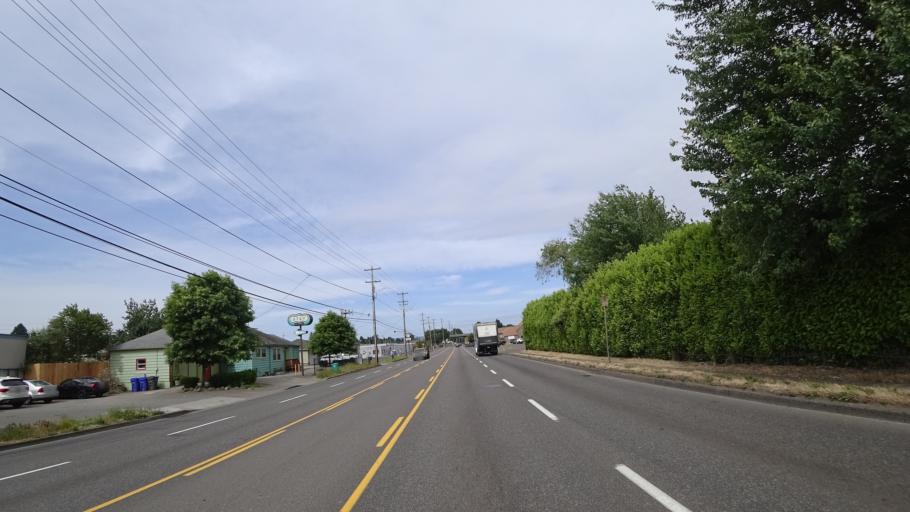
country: US
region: Oregon
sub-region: Multnomah County
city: Portland
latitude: 45.5728
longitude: -122.6258
